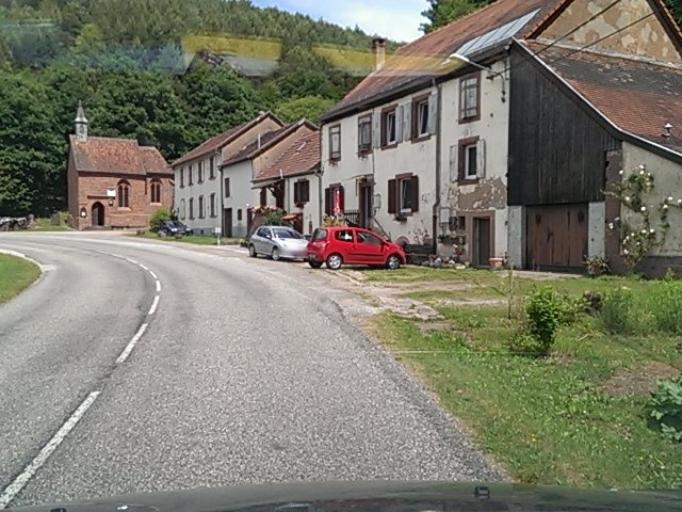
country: FR
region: Lorraine
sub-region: Departement de la Moselle
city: Bitche
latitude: 48.9886
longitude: 7.4441
